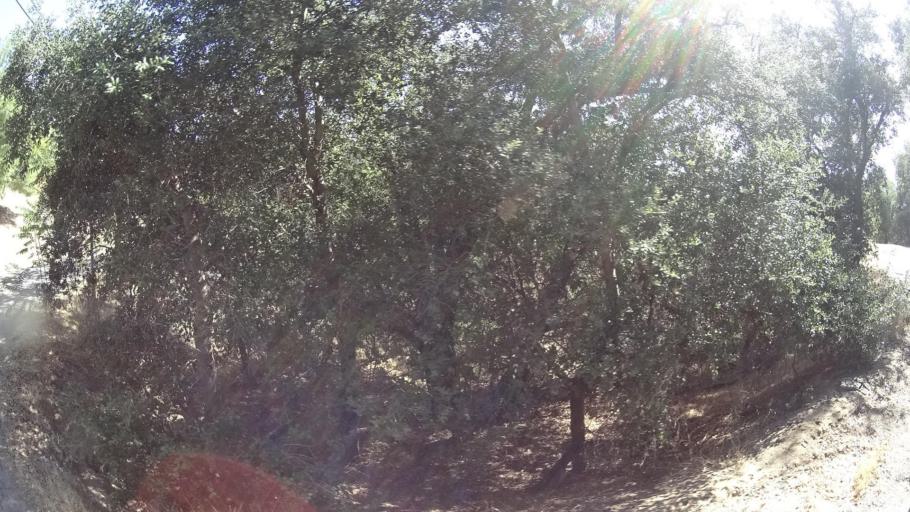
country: US
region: California
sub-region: San Diego County
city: Julian
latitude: 33.0793
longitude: -116.6111
